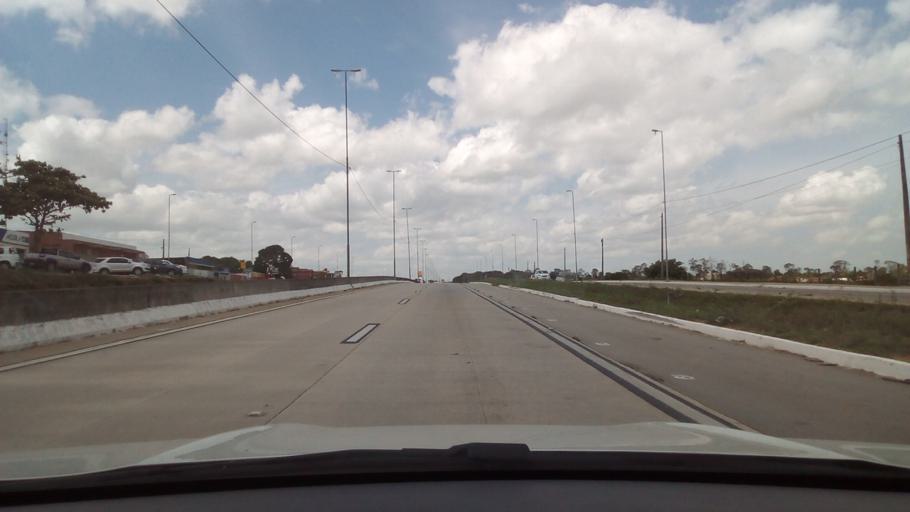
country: BR
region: Paraiba
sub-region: Mamanguape
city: Mamanguape
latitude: -6.8340
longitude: -35.1370
